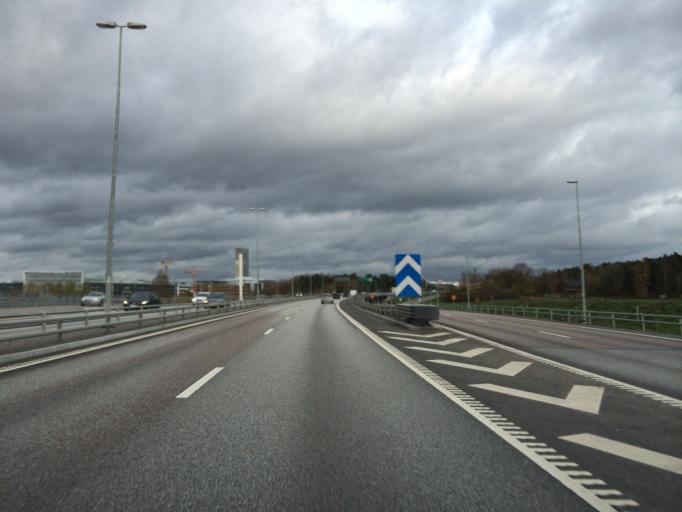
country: SE
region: Stockholm
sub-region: Stockholms Kommun
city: Kista
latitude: 59.3946
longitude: 17.9505
